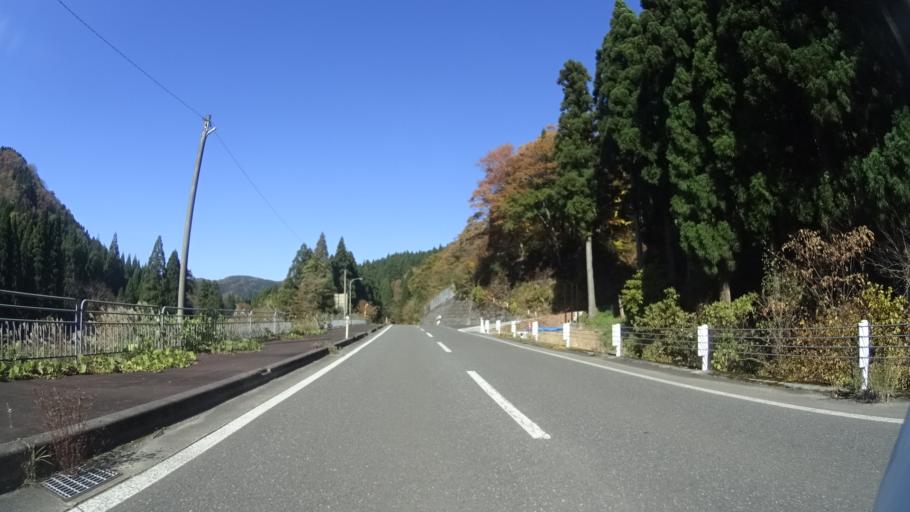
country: JP
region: Fukui
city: Ono
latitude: 35.8657
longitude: 136.3627
